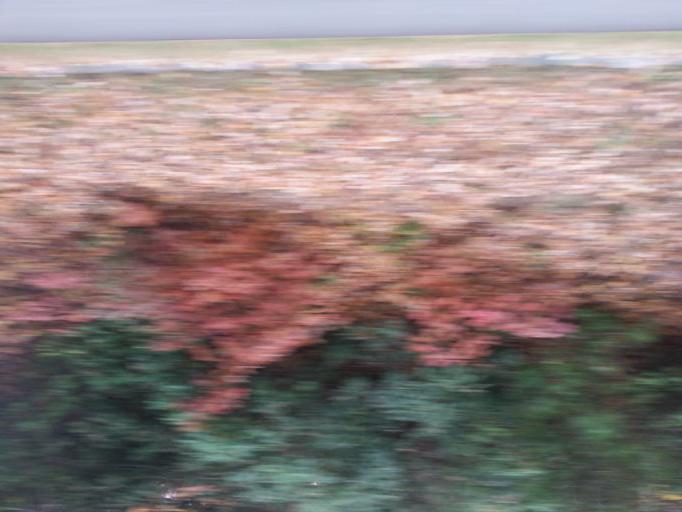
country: US
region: North Carolina
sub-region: Ashe County
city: Jefferson
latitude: 36.3141
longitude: -81.3638
